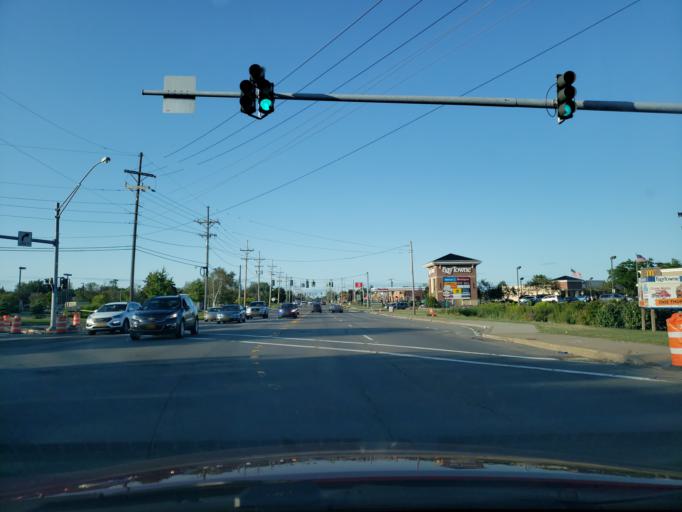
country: US
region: New York
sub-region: Monroe County
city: Brighton
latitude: 43.1898
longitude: -77.5039
